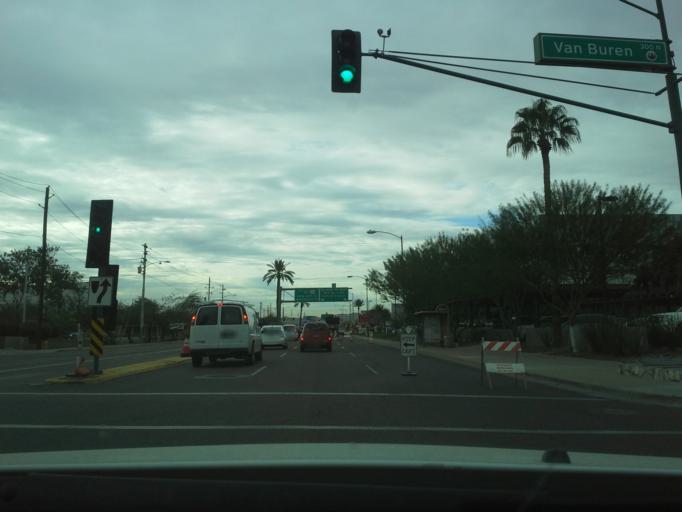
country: US
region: Arizona
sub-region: Maricopa County
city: Tempe Junction
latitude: 33.4512
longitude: -111.9872
